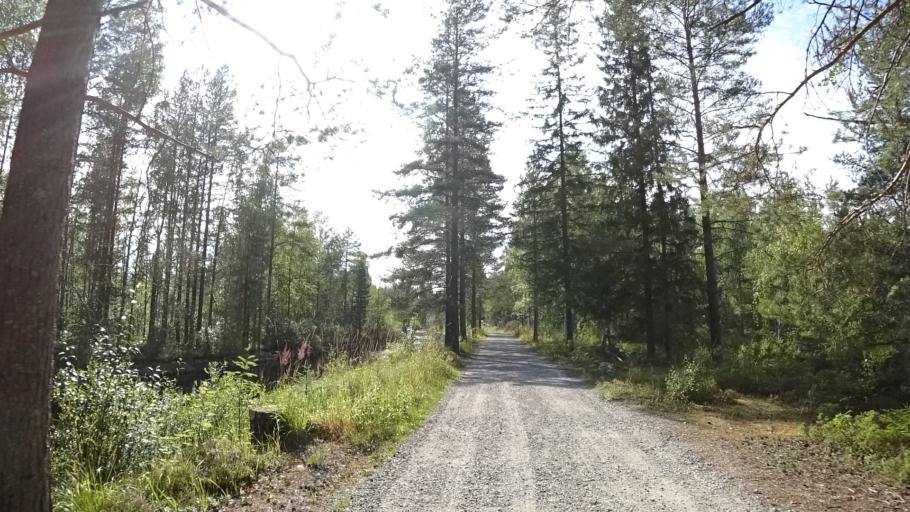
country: FI
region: North Karelia
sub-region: Joensuu
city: Eno
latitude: 62.8002
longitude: 30.1369
